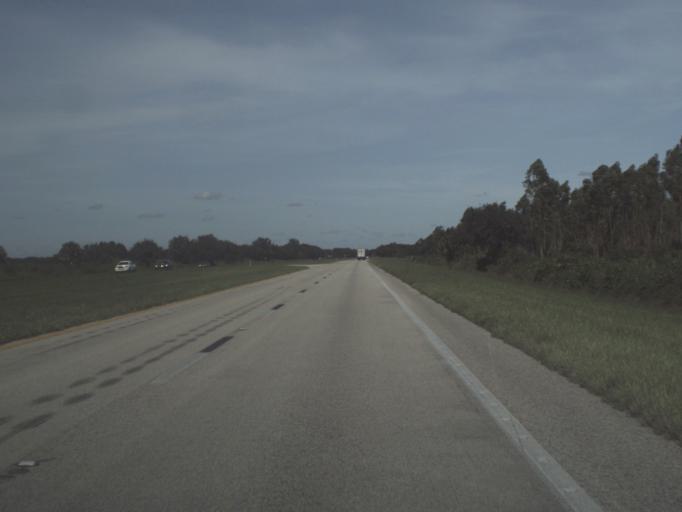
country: US
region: Florida
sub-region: Highlands County
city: Placid Lakes
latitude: 27.0182
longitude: -81.3372
